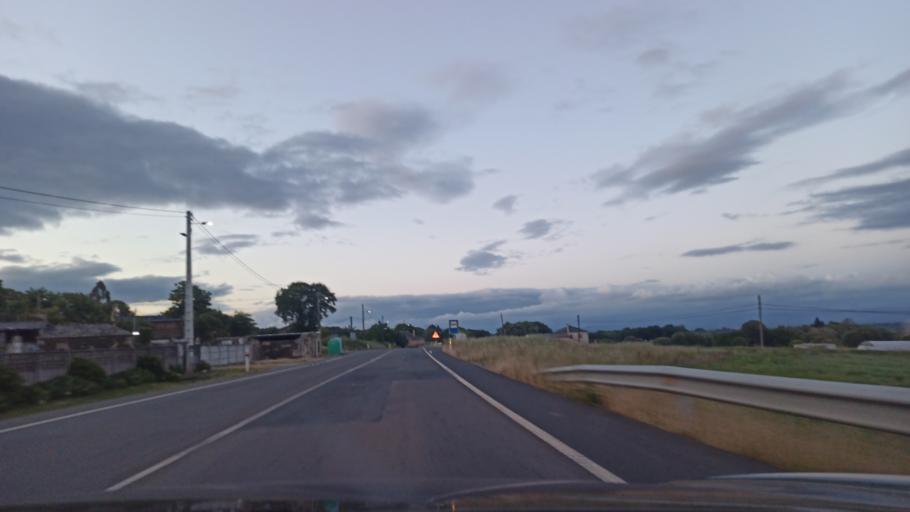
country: ES
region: Galicia
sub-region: Provincia de Lugo
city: Ourol
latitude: 42.9445
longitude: -7.6267
